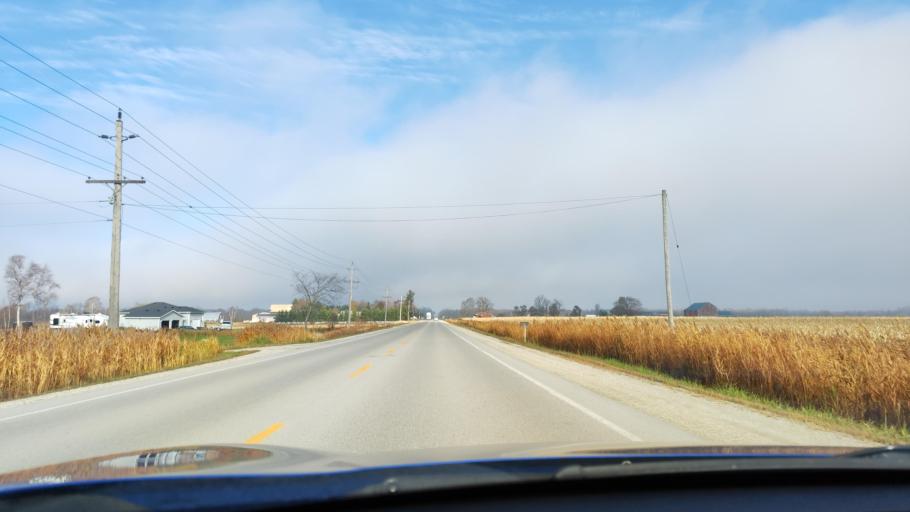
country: CA
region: Ontario
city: Wasaga Beach
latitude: 44.4514
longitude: -80.0703
